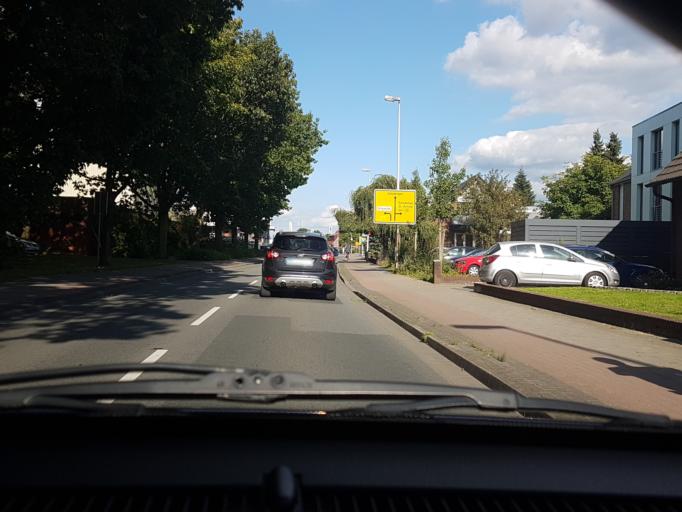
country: DE
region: North Rhine-Westphalia
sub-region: Regierungsbezirk Munster
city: Neuenkirchen
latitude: 52.2385
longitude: 7.3731
